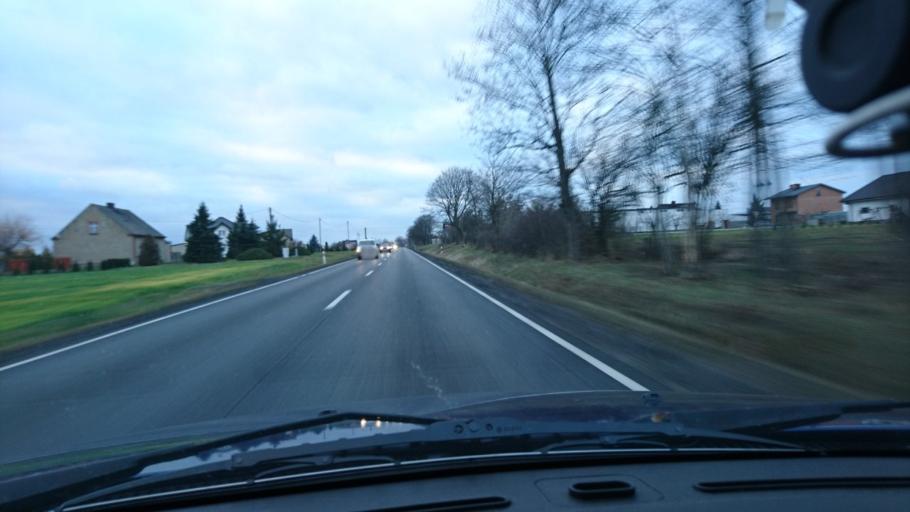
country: PL
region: Greater Poland Voivodeship
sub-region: Powiat kepinski
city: Slupia pod Kepnem
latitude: 51.2362
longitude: 18.0512
